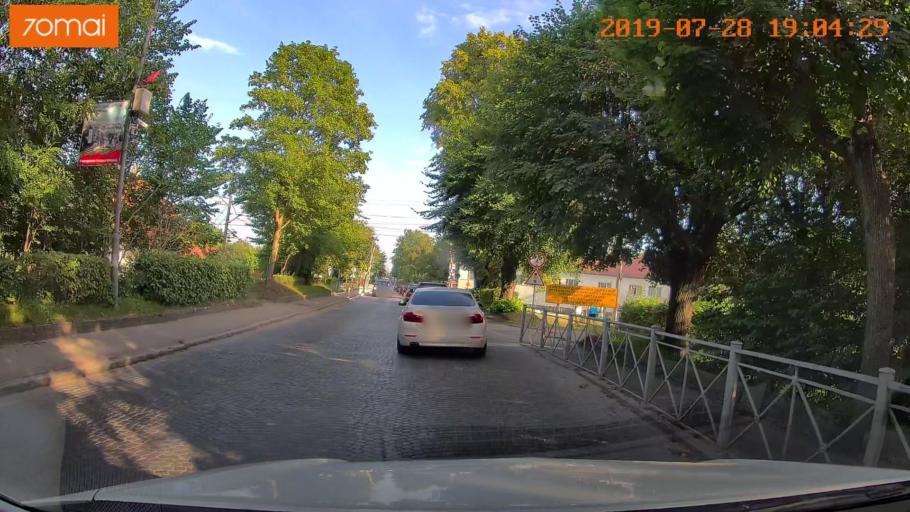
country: RU
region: Kaliningrad
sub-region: Gorod Svetlogorsk
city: Svetlogorsk
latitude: 54.9338
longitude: 20.1615
